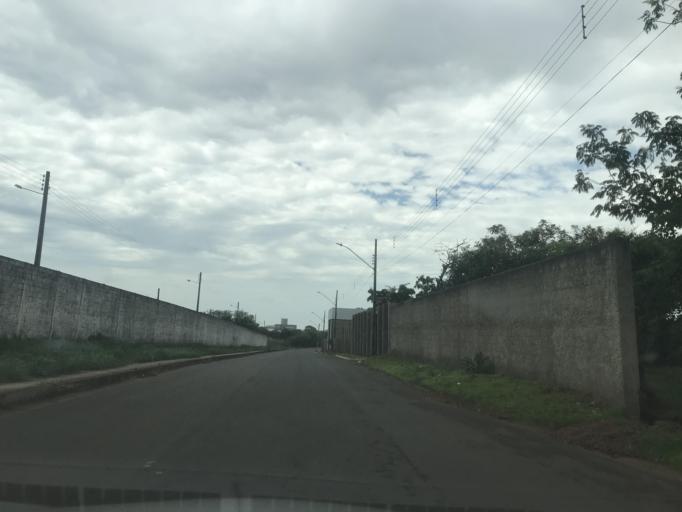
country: BR
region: Goias
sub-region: Luziania
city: Luziania
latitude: -16.2591
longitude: -47.9755
